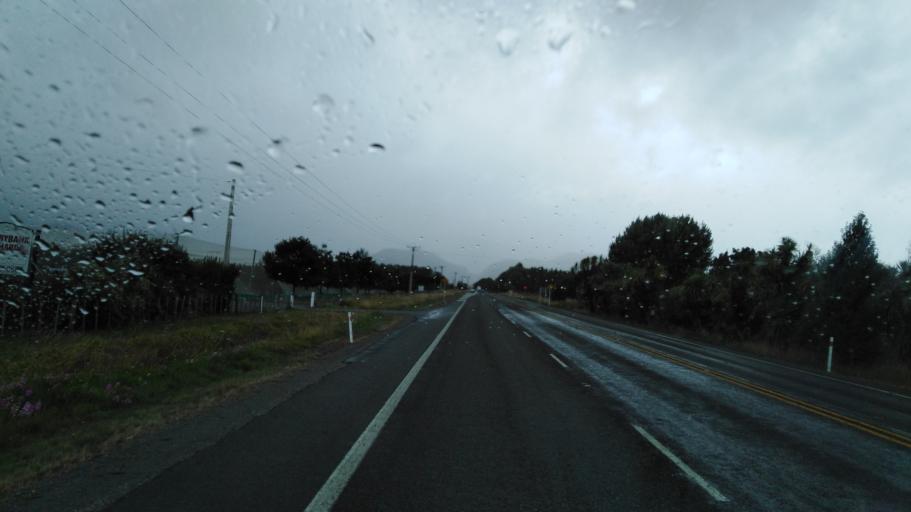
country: NZ
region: Marlborough
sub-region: Marlborough District
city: Blenheim
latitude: -41.4531
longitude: 173.9631
